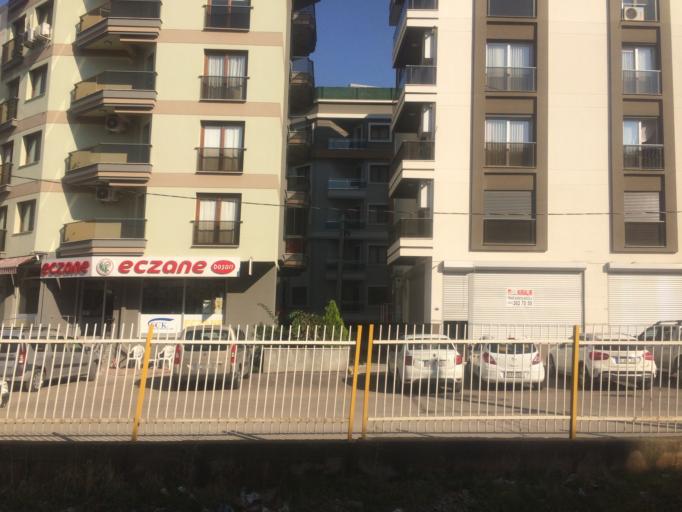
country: TR
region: Izmir
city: Karsiyaka
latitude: 38.4722
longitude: 27.0926
